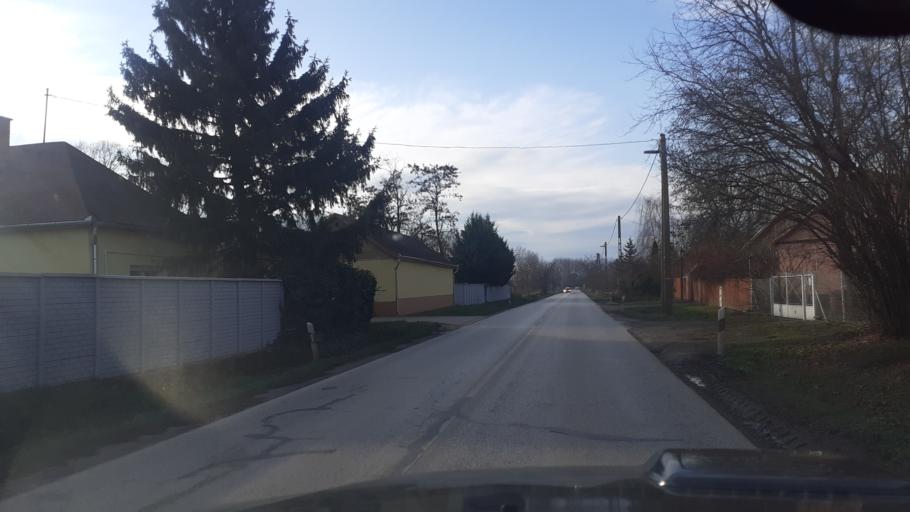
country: HU
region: Bacs-Kiskun
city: Tass
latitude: 47.0202
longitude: 19.0498
